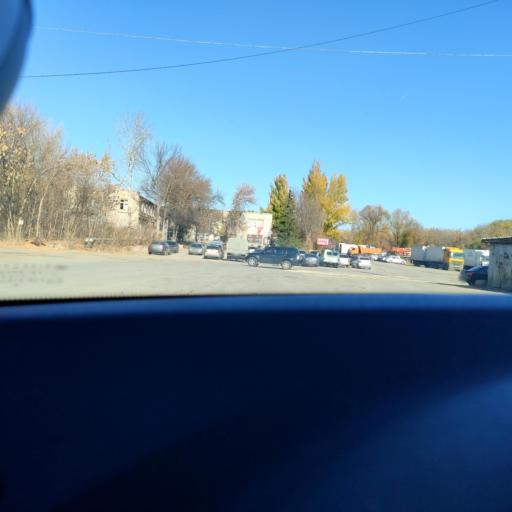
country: RU
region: Samara
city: Petra-Dubrava
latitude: 53.2585
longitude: 50.2986
